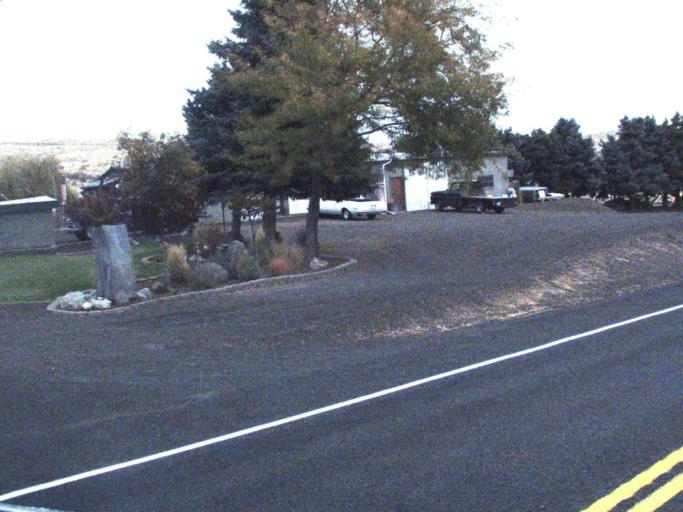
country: US
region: Washington
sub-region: Adams County
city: Ritzville
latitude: 46.7586
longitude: -118.3124
